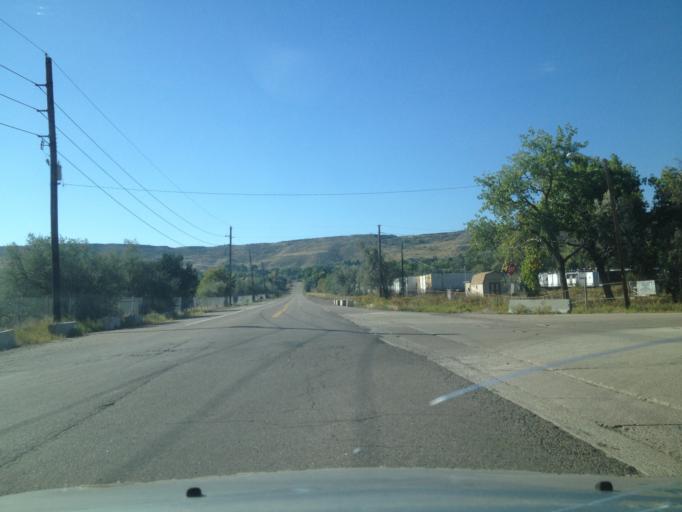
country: US
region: Colorado
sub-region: Jefferson County
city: Applewood
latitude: 39.7681
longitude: -105.1748
